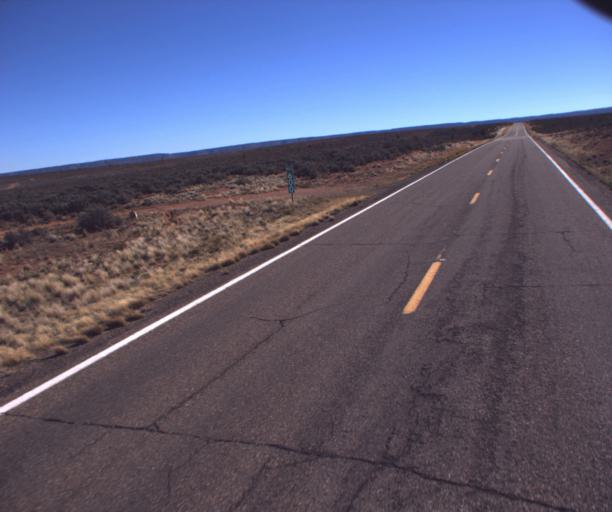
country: US
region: Arizona
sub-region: Coconino County
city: Fredonia
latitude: 36.8998
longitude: -112.3748
